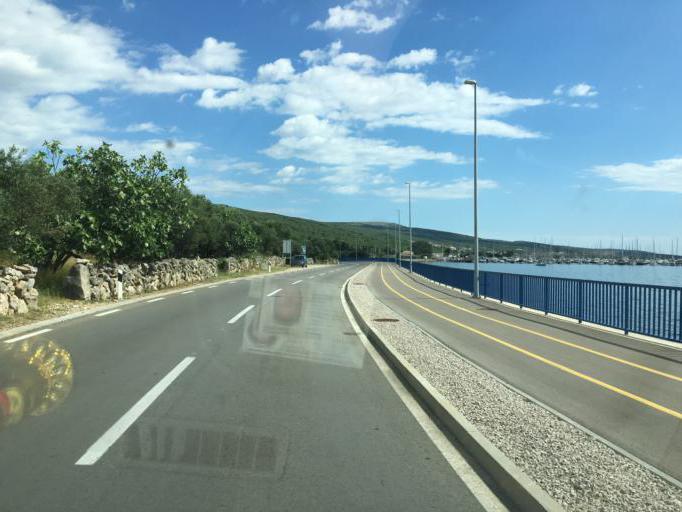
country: HR
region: Primorsko-Goranska
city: Punat
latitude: 45.0382
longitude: 14.6269
